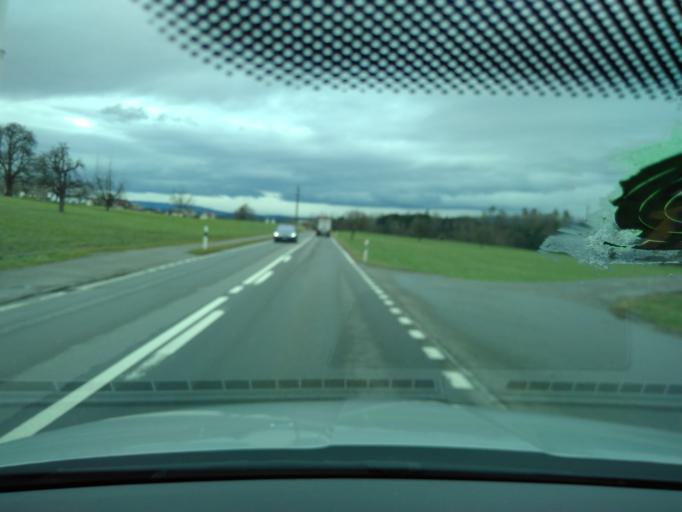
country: CH
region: Lucerne
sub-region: Hochdorf District
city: Ballwil
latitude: 47.1268
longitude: 8.3042
